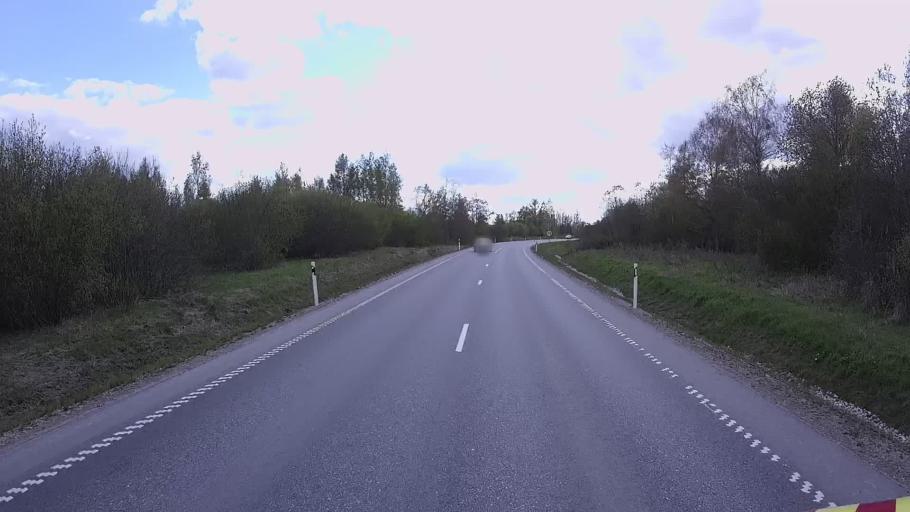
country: EE
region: Jogevamaa
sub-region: Mustvee linn
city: Mustvee
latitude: 58.8223
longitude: 26.7471
